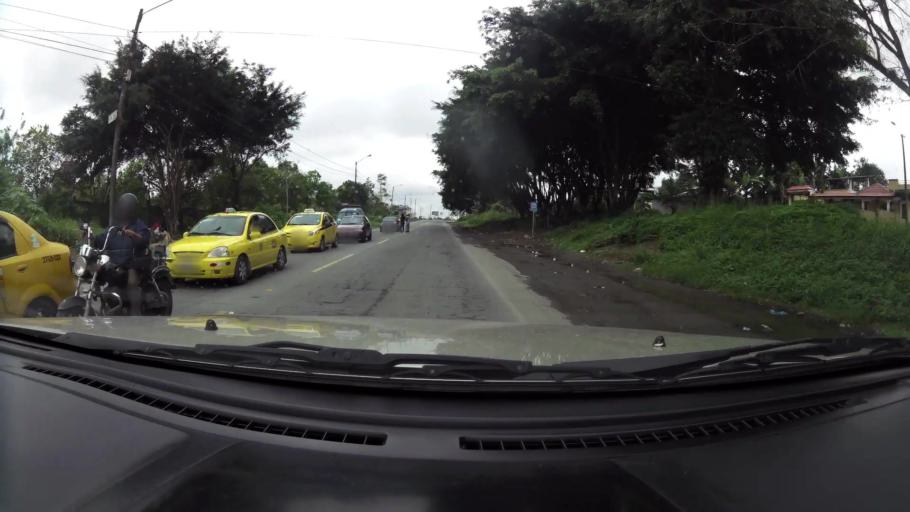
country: EC
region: Santo Domingo de los Tsachilas
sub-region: Canton Santo Domingo de los Colorados
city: Santo Domingo de los Colorados
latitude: -0.2820
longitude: -79.1840
